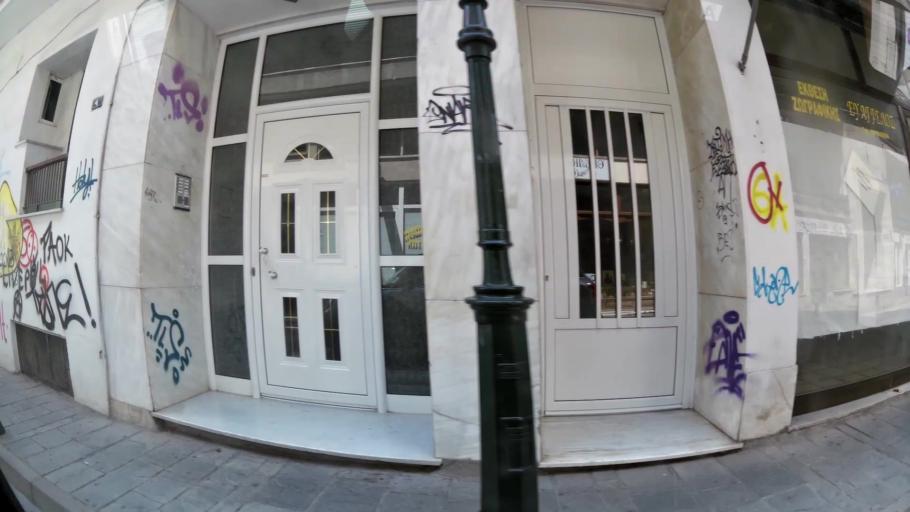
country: GR
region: West Macedonia
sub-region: Nomos Kozanis
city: Kozani
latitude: 40.3001
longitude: 21.7871
